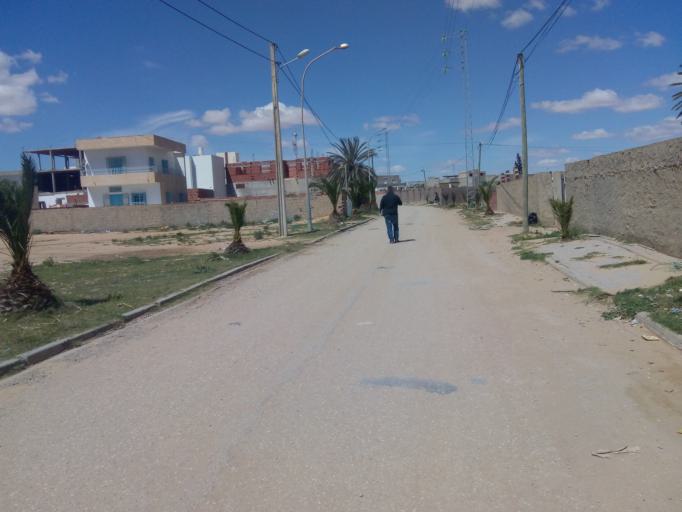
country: TN
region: Safaqis
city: Sfax
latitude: 34.7424
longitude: 10.5304
